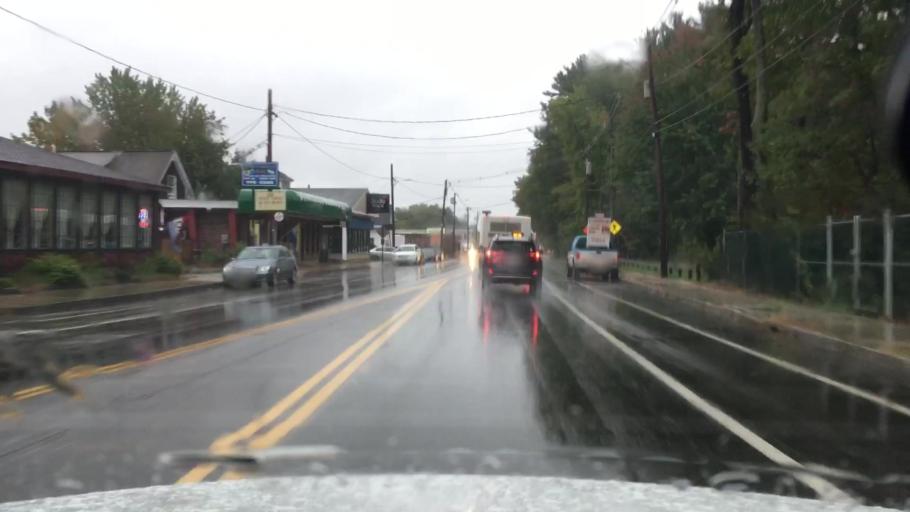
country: US
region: Maine
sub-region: Cumberland County
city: Portland
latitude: 43.6773
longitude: -70.2877
